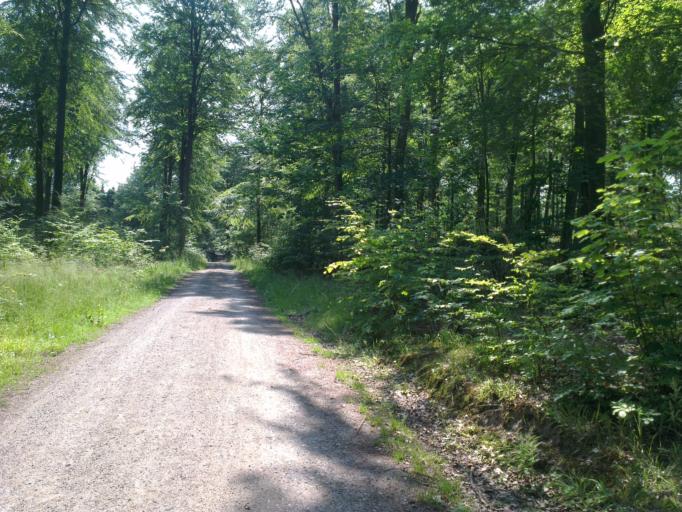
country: DK
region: Capital Region
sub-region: Hillerod Kommune
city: Hillerod
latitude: 55.9216
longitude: 12.3469
